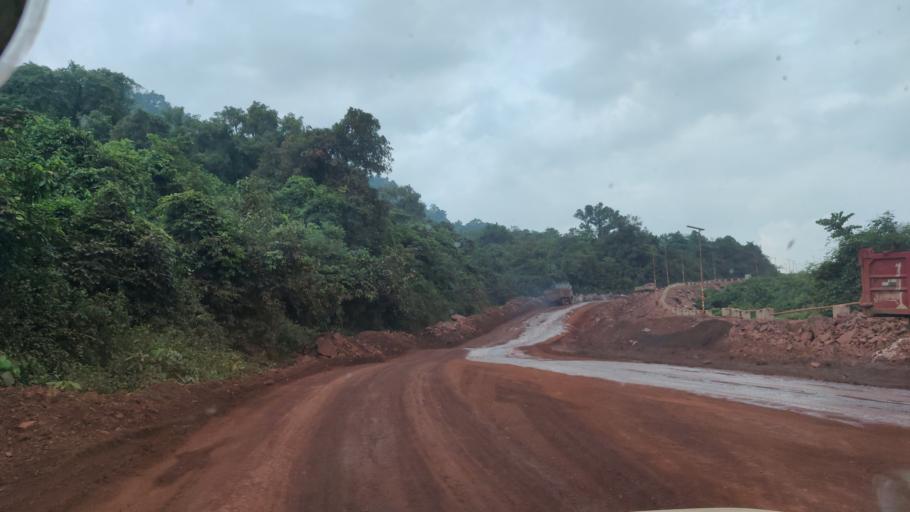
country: IN
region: Odisha
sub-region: Kendujhar
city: Barbil
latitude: 21.6245
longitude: 85.5121
